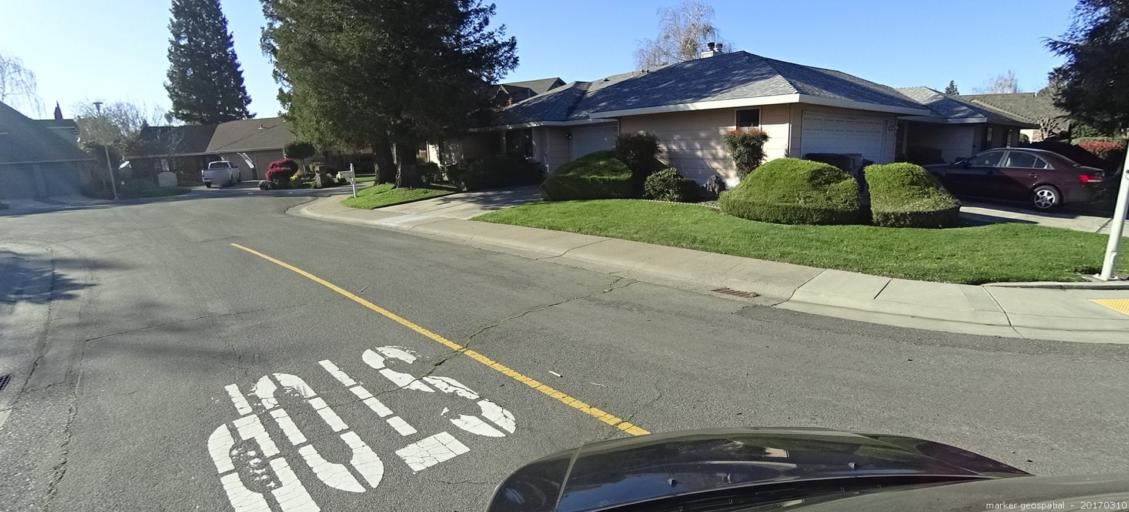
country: US
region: California
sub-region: Sacramento County
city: Parkway
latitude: 38.4985
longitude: -121.5307
